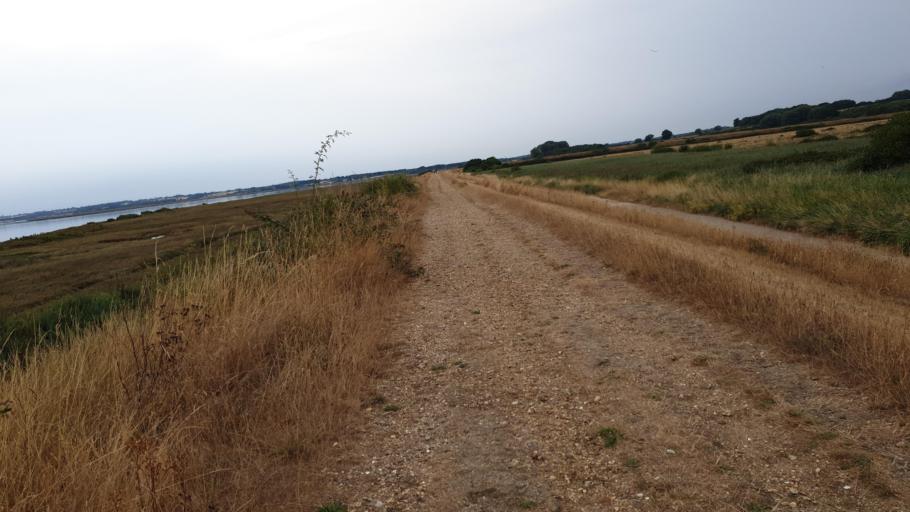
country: GB
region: England
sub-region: Essex
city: Brightlingsea
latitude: 51.8125
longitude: 1.0013
